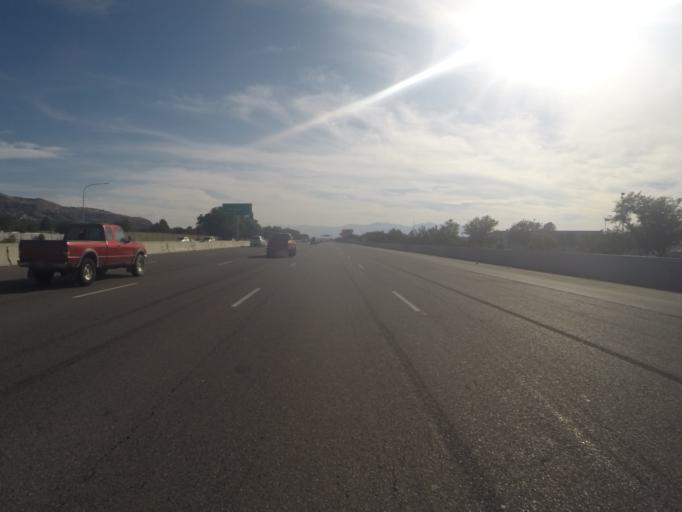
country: US
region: Utah
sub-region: Davis County
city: North Salt Lake
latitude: 40.8585
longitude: -111.9050
